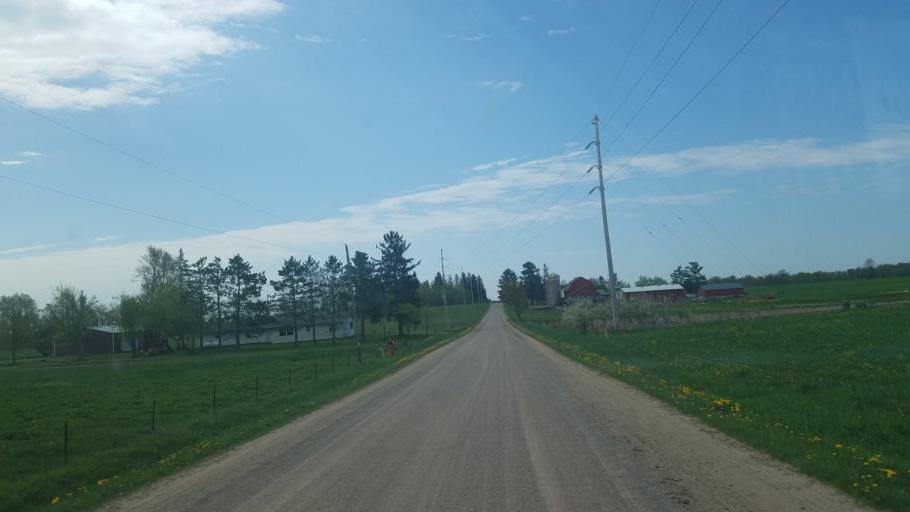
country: US
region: Wisconsin
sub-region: Marathon County
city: Spencer
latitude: 44.6236
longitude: -90.3766
